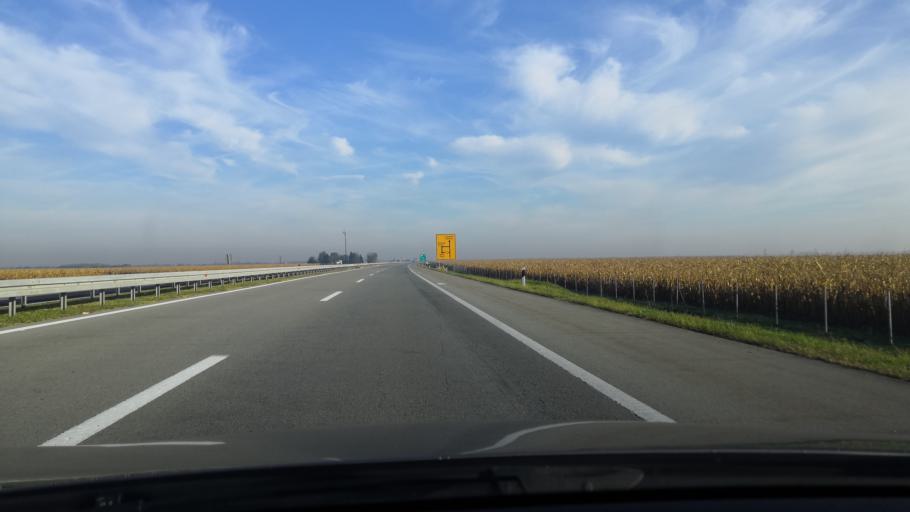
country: RS
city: Stepanovicevo
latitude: 45.4195
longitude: 19.7370
